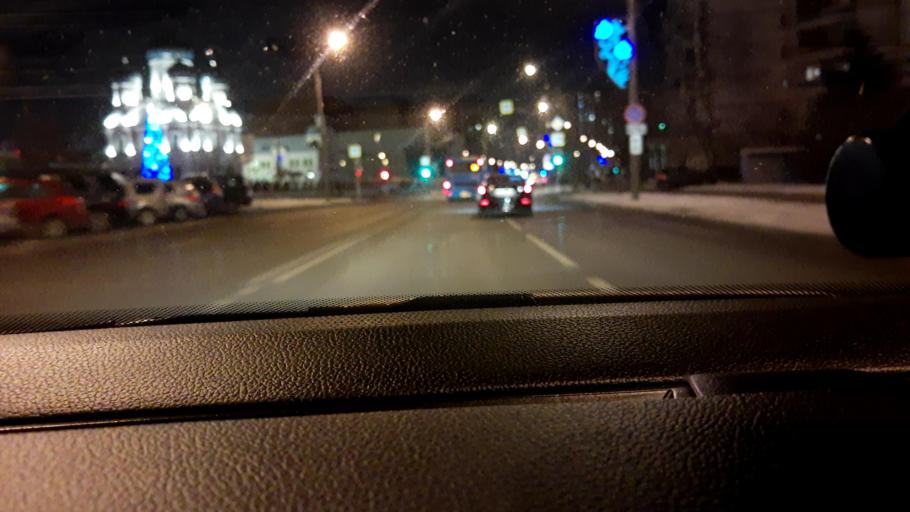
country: RU
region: Moskovskaya
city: Shcherbinka
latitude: 55.5435
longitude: 37.5406
